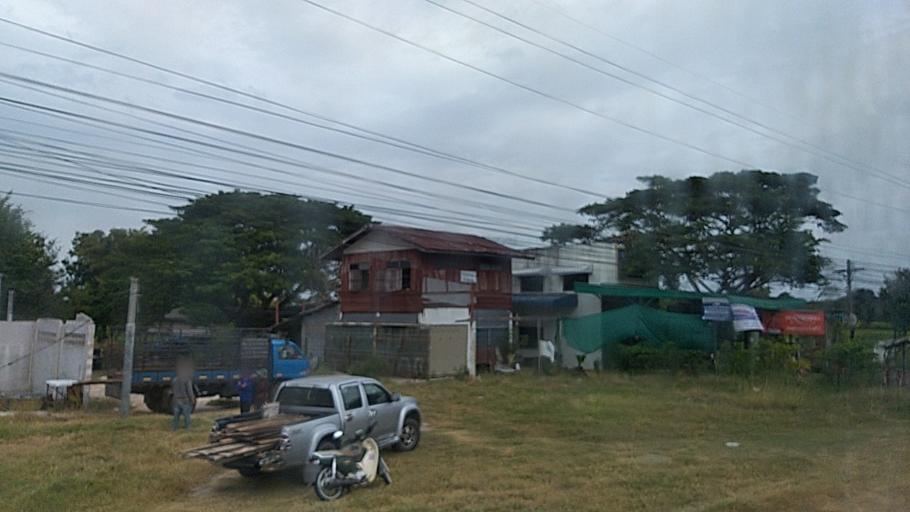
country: TH
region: Roi Et
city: Changhan
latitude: 16.0825
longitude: 103.5715
